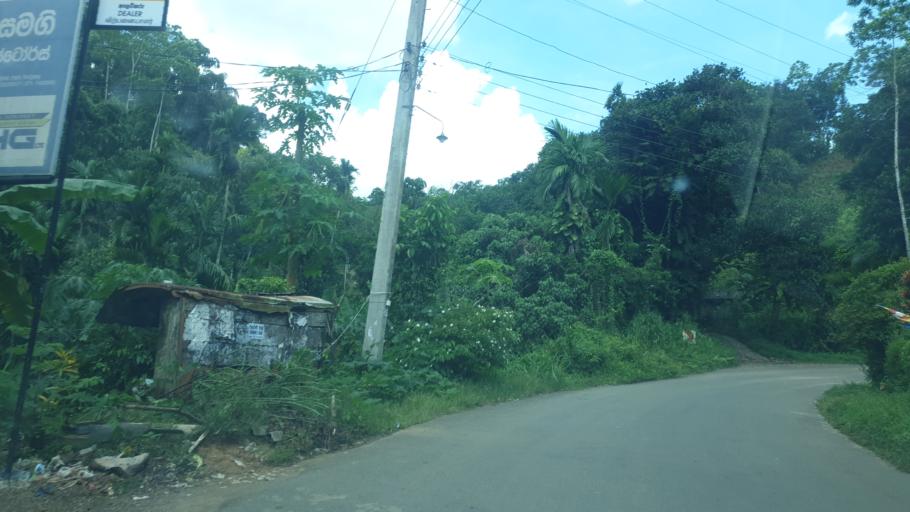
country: LK
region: Sabaragamuwa
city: Ratnapura
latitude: 6.4790
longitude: 80.4165
